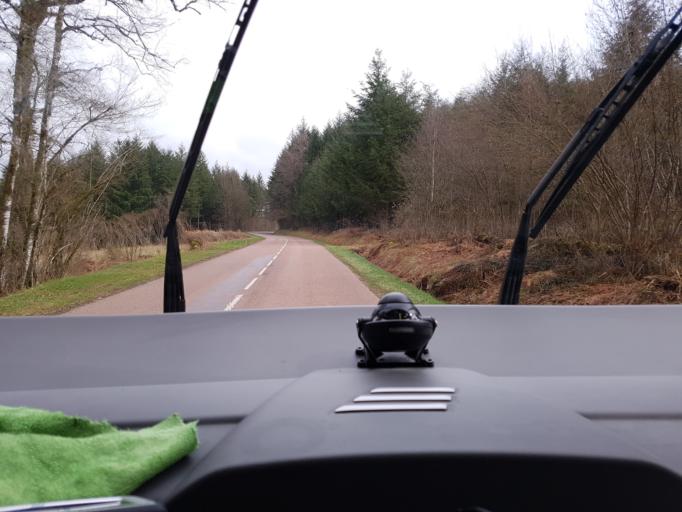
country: FR
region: Bourgogne
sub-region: Departement de la Nievre
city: Chateau-Chinon(Ville)
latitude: 47.2234
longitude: 4.0326
